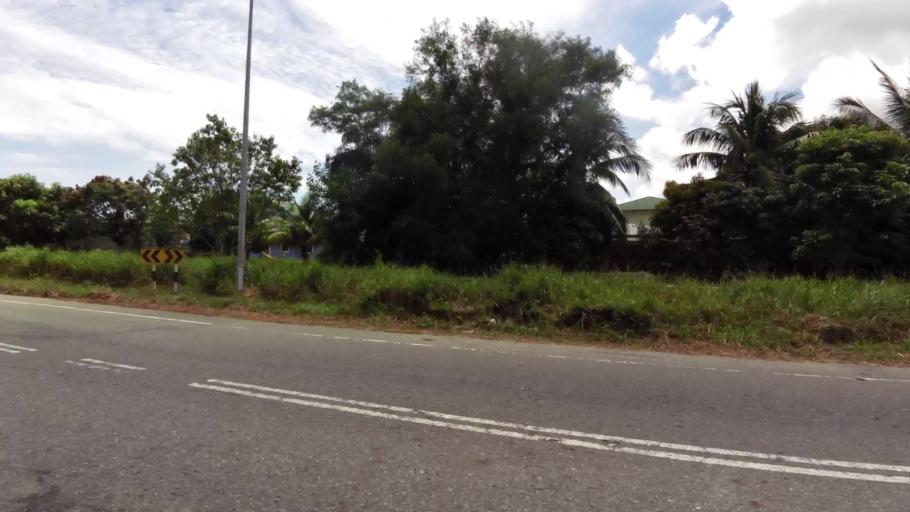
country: BN
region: Brunei and Muara
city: Bandar Seri Begawan
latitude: 4.9573
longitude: 114.9039
